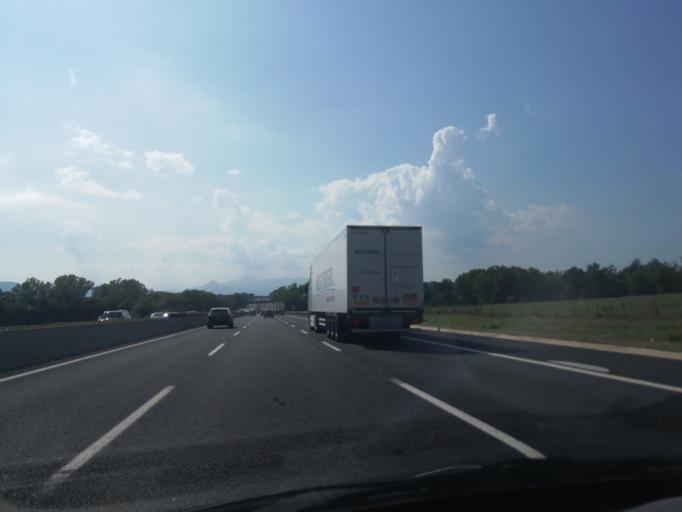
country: IT
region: Latium
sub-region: Provincia di Frosinone
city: Pofi
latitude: 41.5506
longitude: 13.4549
